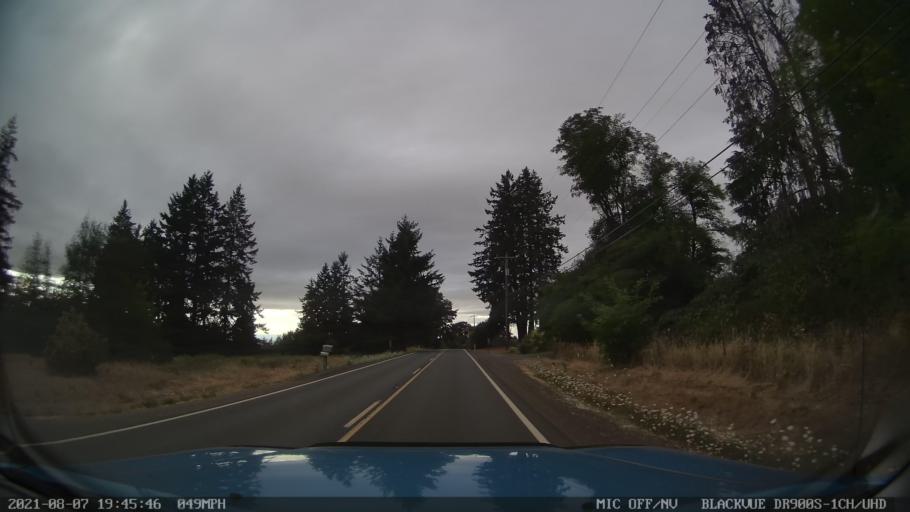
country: US
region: Oregon
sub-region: Marion County
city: Silverton
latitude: 44.9515
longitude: -122.6987
